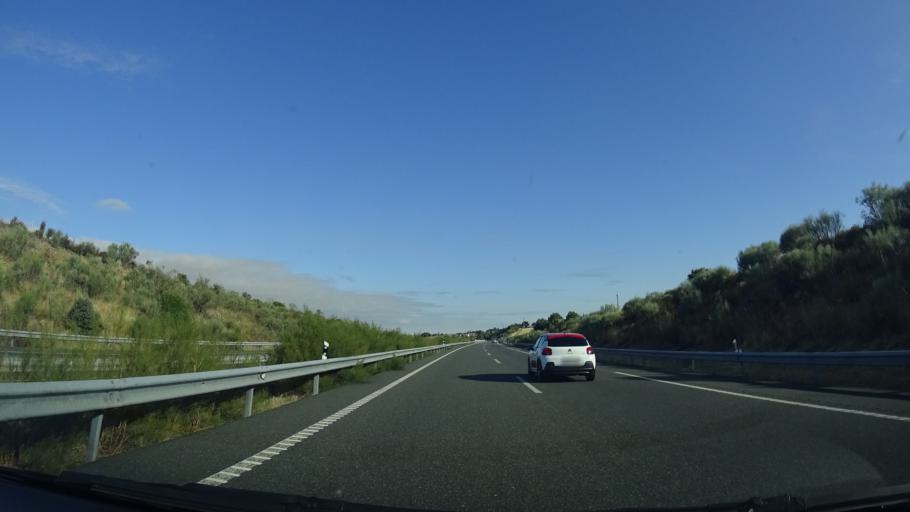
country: ES
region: Castille and Leon
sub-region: Provincia de Segovia
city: Labajos
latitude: 40.8487
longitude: -4.5428
